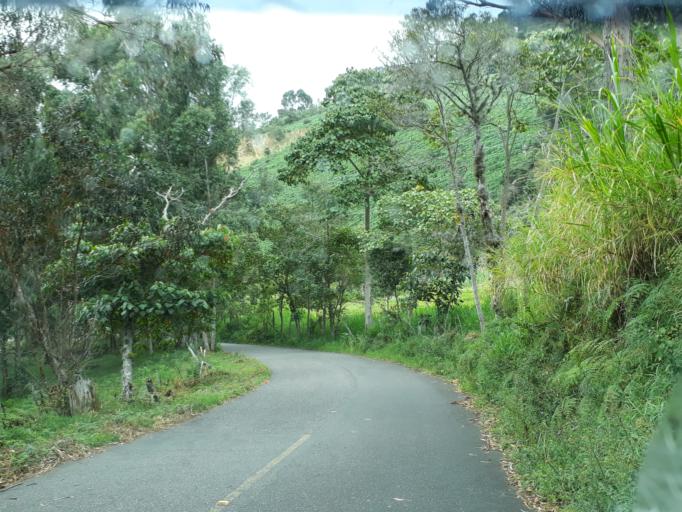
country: CO
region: Cundinamarca
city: Cabrera
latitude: 4.0157
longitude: -74.5102
